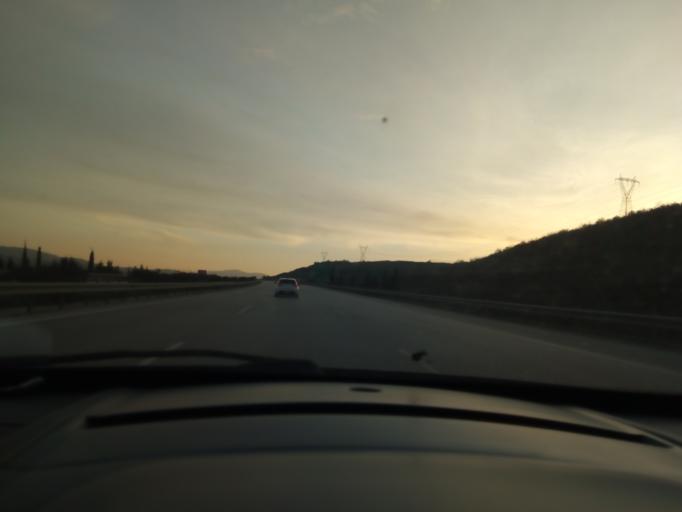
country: TR
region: Bursa
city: Niluefer
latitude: 40.2747
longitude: 28.9747
